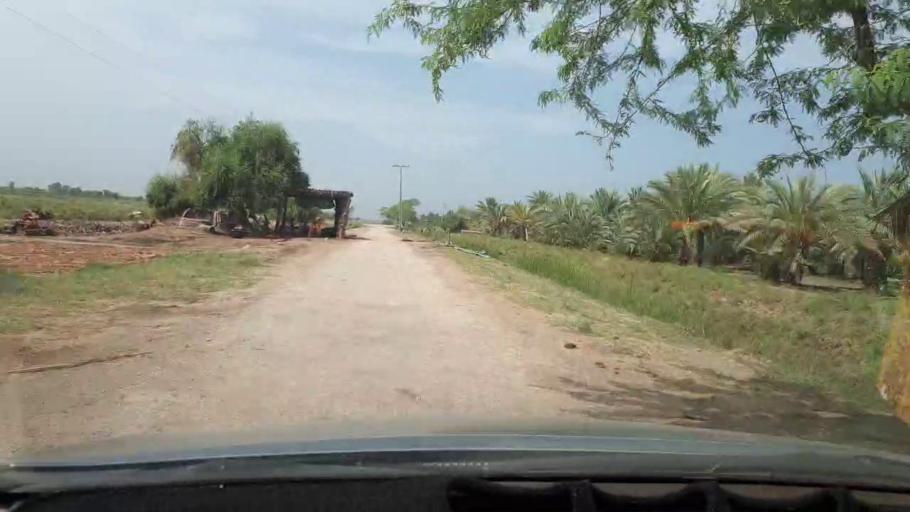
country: PK
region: Sindh
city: Khairpur
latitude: 27.4747
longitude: 68.7431
